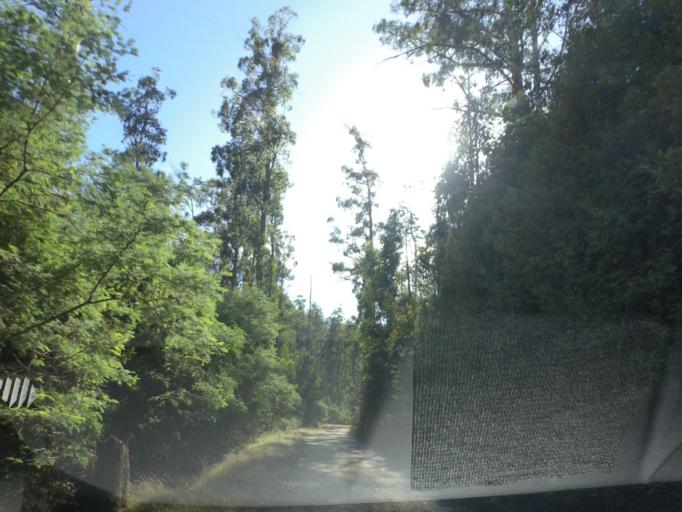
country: AU
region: Victoria
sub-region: Yarra Ranges
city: Millgrove
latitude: -37.5018
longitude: 145.8225
